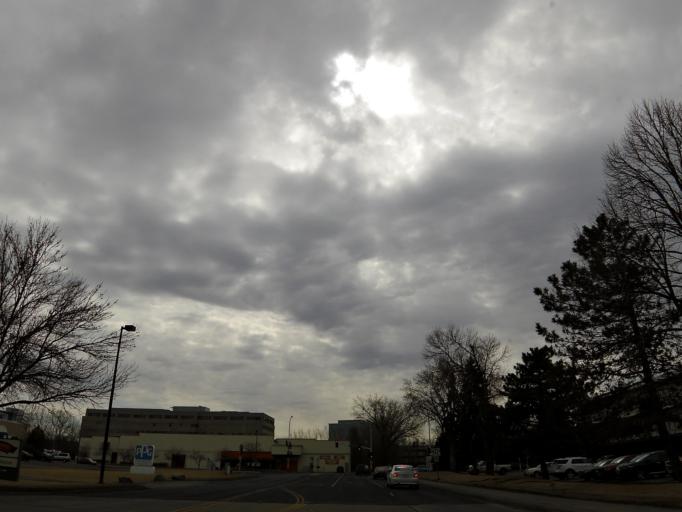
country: US
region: Minnesota
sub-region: Hennepin County
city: Edina
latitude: 44.8642
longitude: -93.3360
